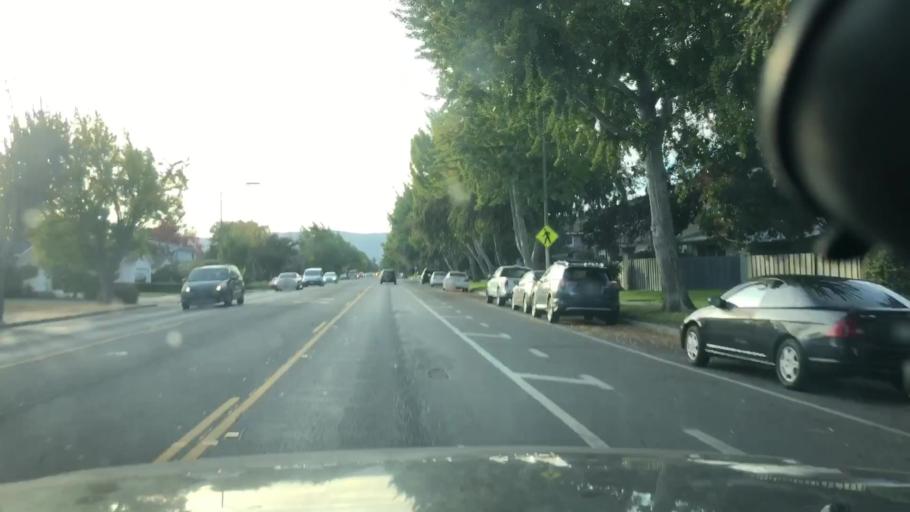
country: US
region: California
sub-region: Santa Clara County
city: Campbell
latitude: 37.3160
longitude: -121.9822
